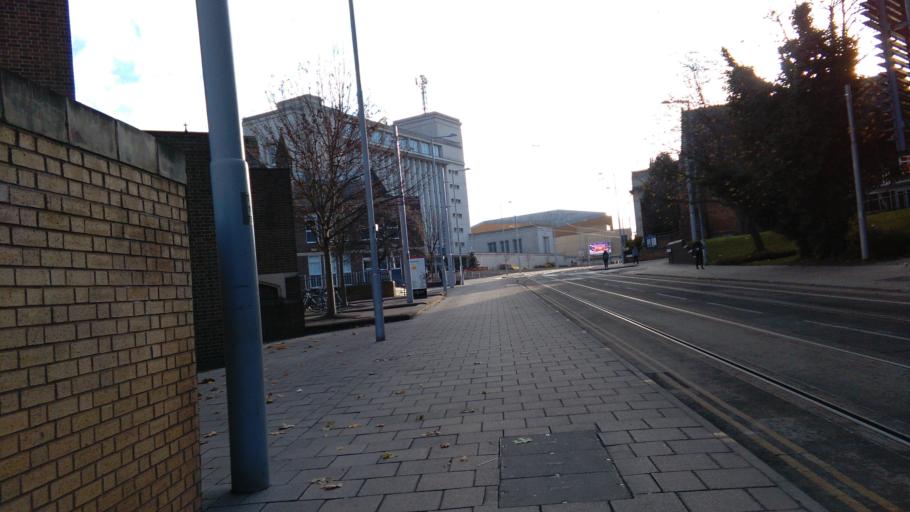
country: GB
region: England
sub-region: Nottingham
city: Nottingham
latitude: 52.9575
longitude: -1.1543
